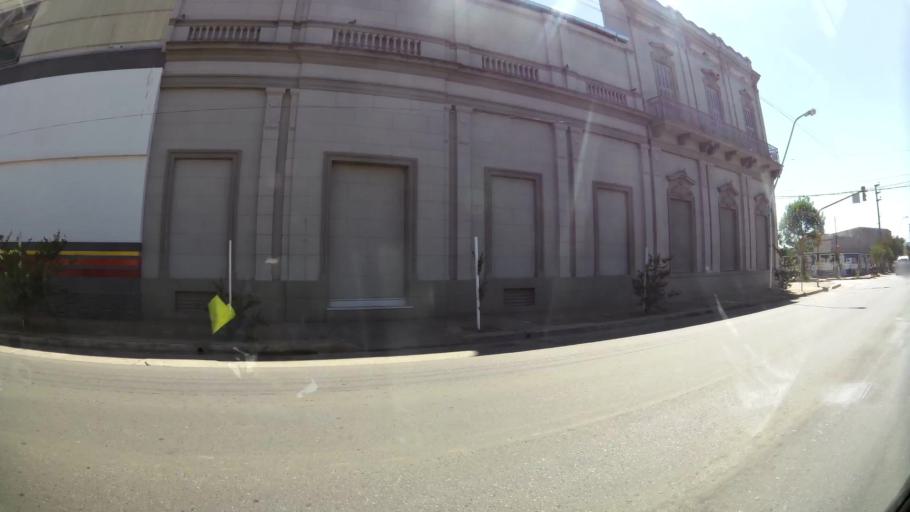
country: AR
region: Santa Fe
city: Esperanza
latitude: -31.4424
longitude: -60.9306
